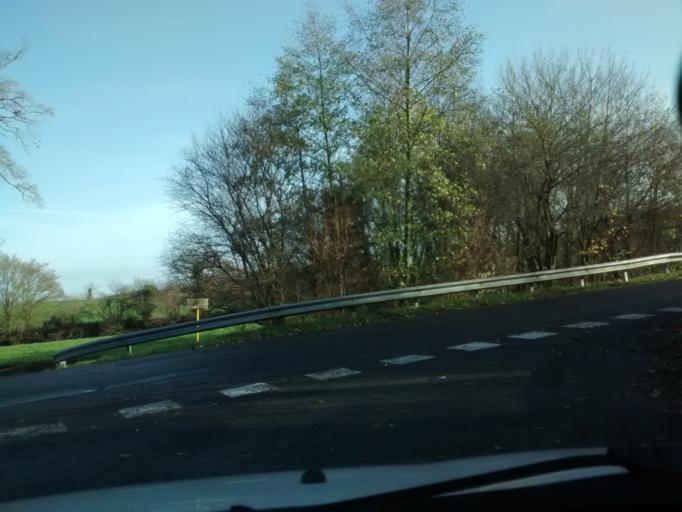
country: FR
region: Brittany
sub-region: Departement d'Ille-et-Vilaine
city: Cesson-Sevigne
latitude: 48.1492
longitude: -1.6129
